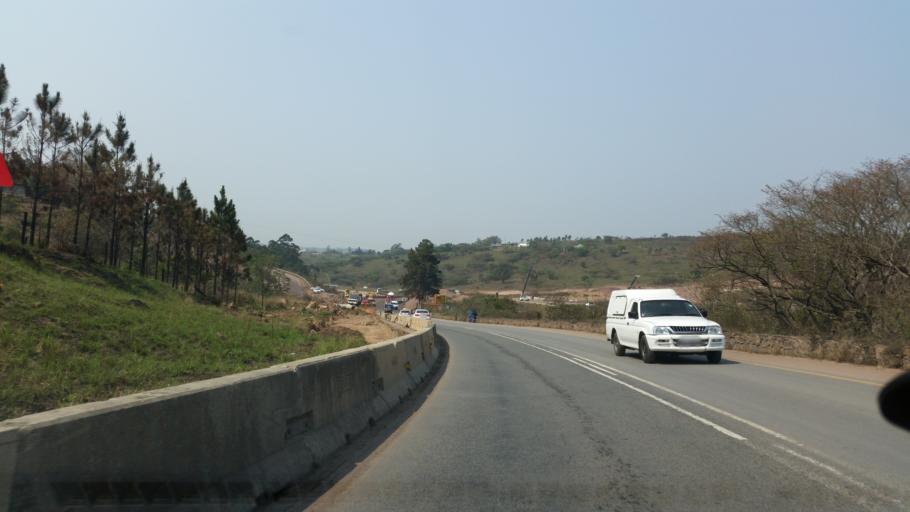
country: ZA
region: KwaZulu-Natal
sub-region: eThekwini Metropolitan Municipality
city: Mpumalanga
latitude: -29.7546
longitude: 30.6658
